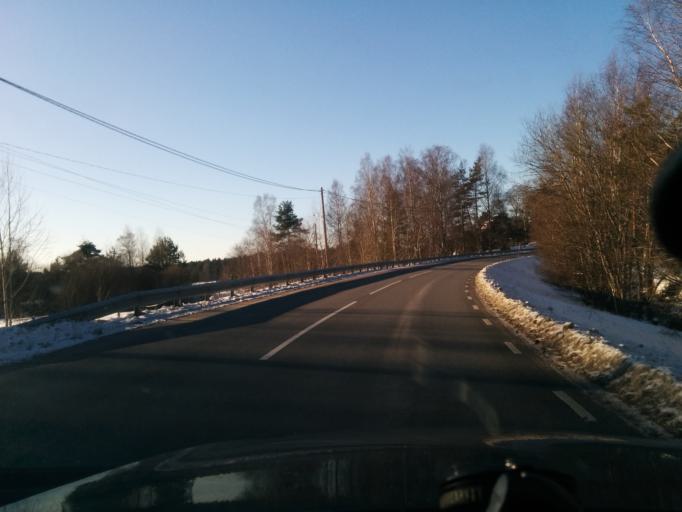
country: SE
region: Stockholm
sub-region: Taby Kommun
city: Taby
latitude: 59.4836
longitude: 18.0901
